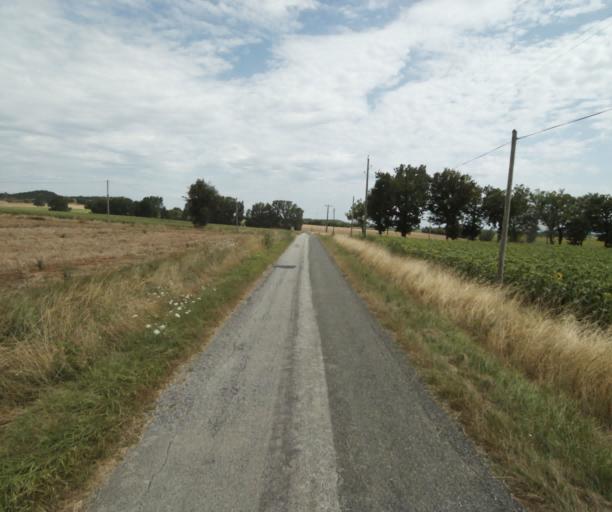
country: FR
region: Midi-Pyrenees
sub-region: Departement de la Haute-Garonne
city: Saint-Felix-Lauragais
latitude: 43.4336
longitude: 1.9034
